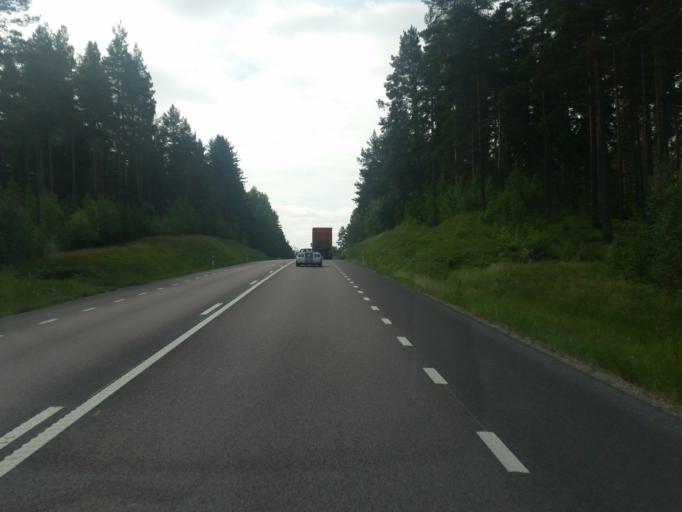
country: SE
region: Dalarna
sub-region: Gagnefs Kommun
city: Gagnef
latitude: 60.6298
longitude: 15.0570
